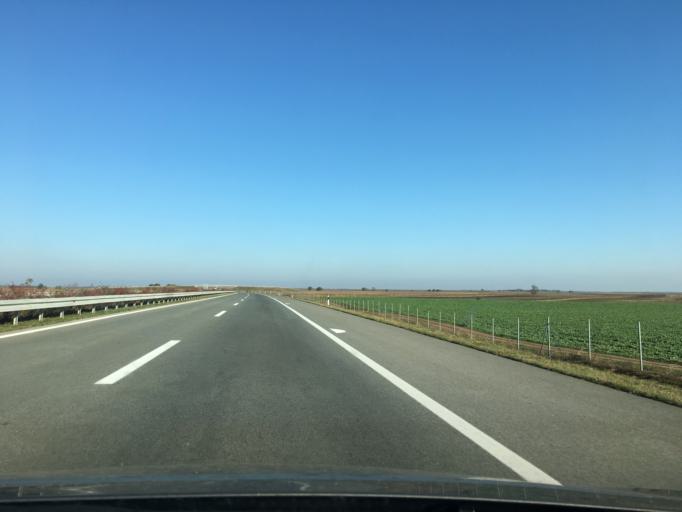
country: RS
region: Autonomna Pokrajina Vojvodina
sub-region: Severnobacki Okrug
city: Mali Igos
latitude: 45.6589
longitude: 19.7254
